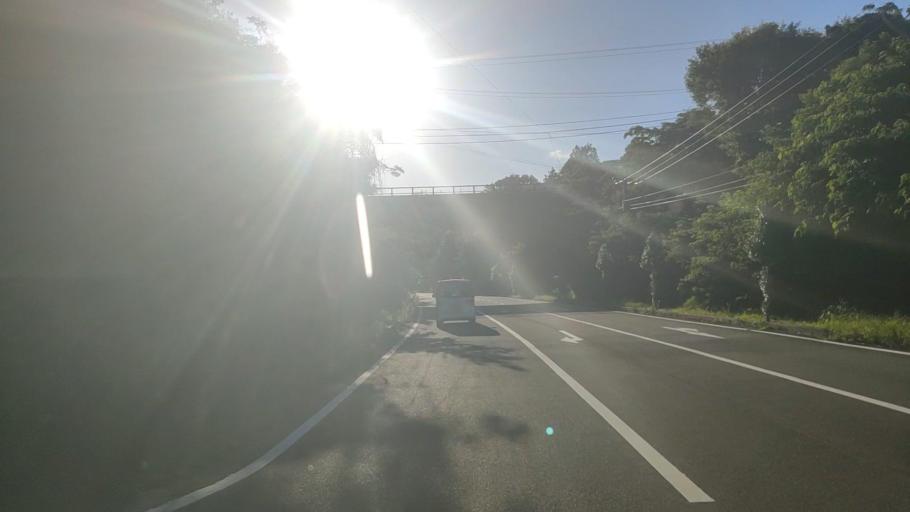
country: JP
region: Mie
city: Toba
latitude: 34.2681
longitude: 136.8087
